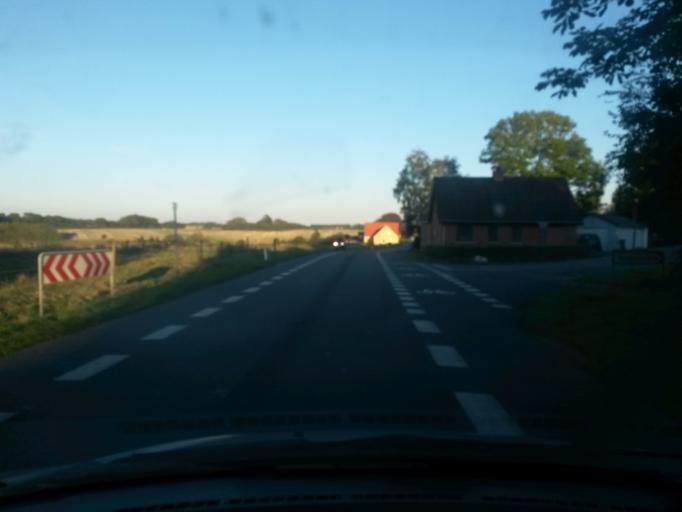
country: DK
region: Central Jutland
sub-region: Silkeborg Kommune
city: Kjellerup
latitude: 56.2893
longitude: 9.3659
